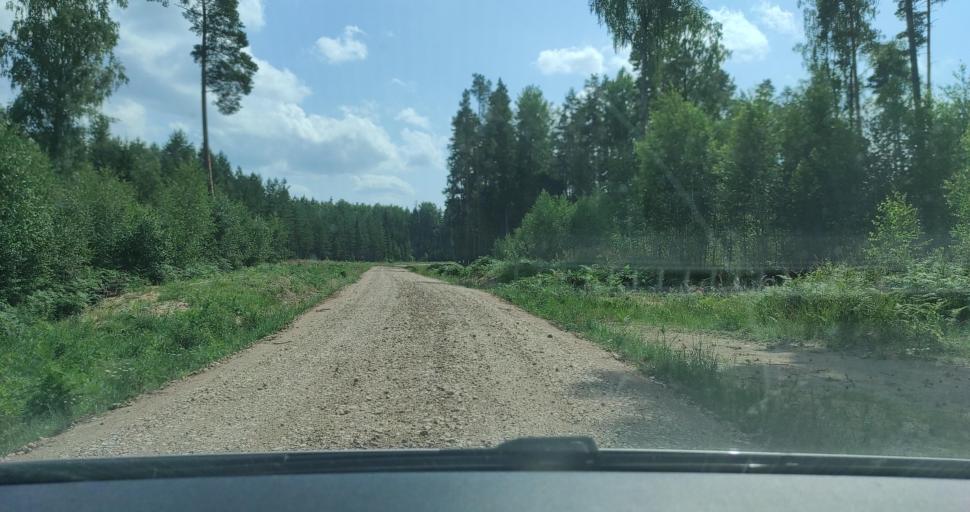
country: LV
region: Kuldigas Rajons
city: Kuldiga
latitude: 57.0637
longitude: 22.1932
